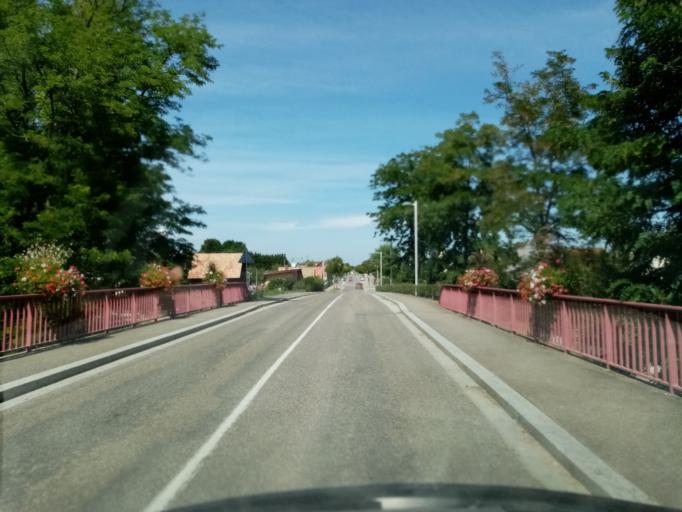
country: FR
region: Alsace
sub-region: Departement du Haut-Rhin
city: Kunheim
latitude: 48.0704
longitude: 7.5340
